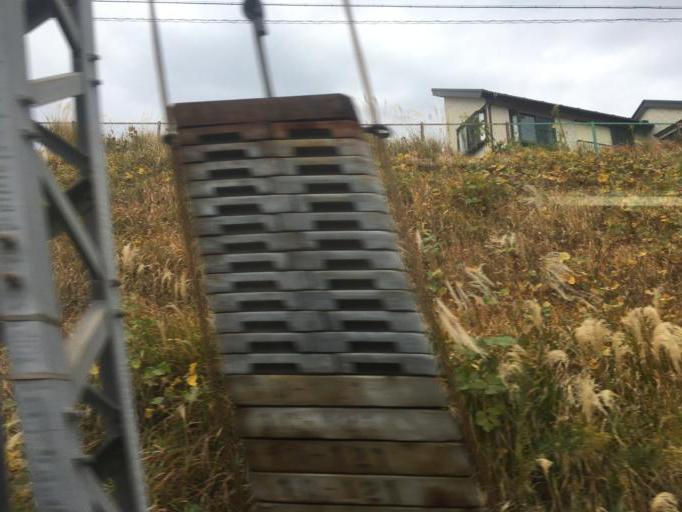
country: JP
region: Chiba
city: Funabashi
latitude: 35.6819
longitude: 140.0291
